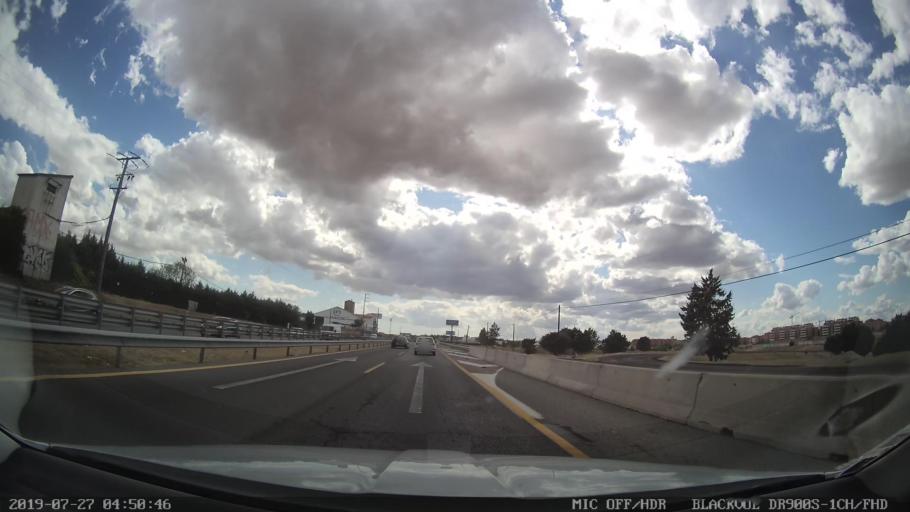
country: ES
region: Madrid
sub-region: Provincia de Madrid
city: Navalcarnero
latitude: 40.2947
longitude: -3.9711
